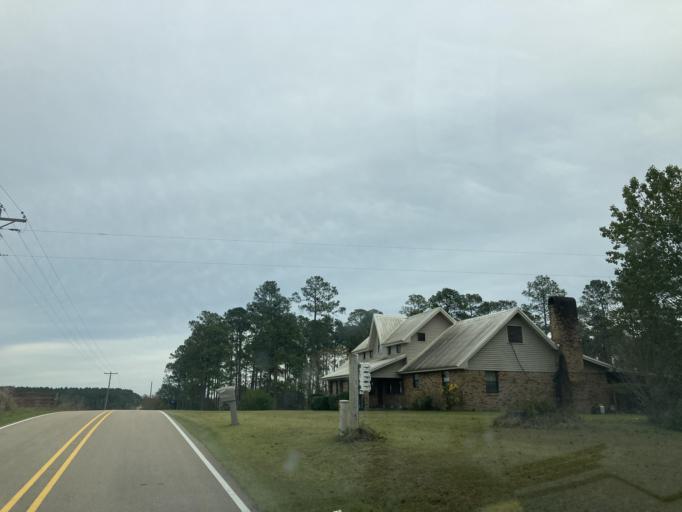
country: US
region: Mississippi
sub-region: Lamar County
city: Lumberton
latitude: 31.0395
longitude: -89.4235
